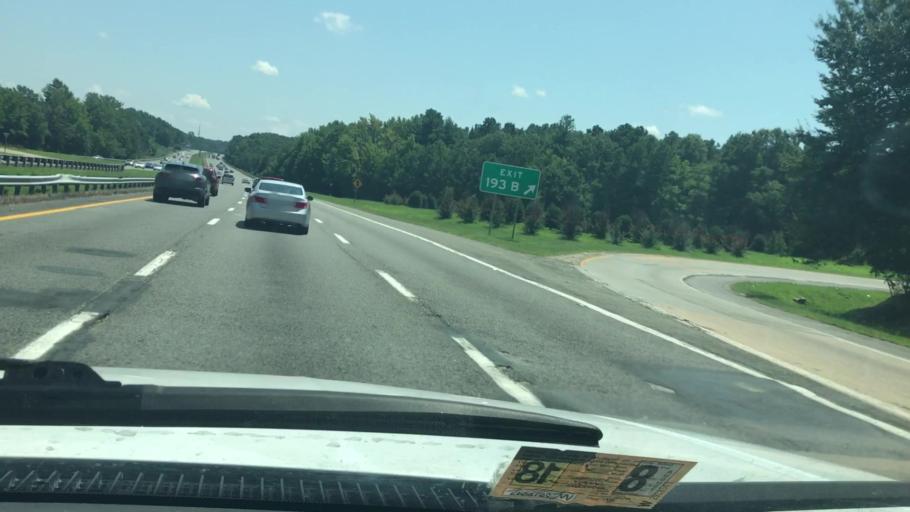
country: US
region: Virginia
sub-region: Henrico County
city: Montrose
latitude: 37.5439
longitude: -77.3933
